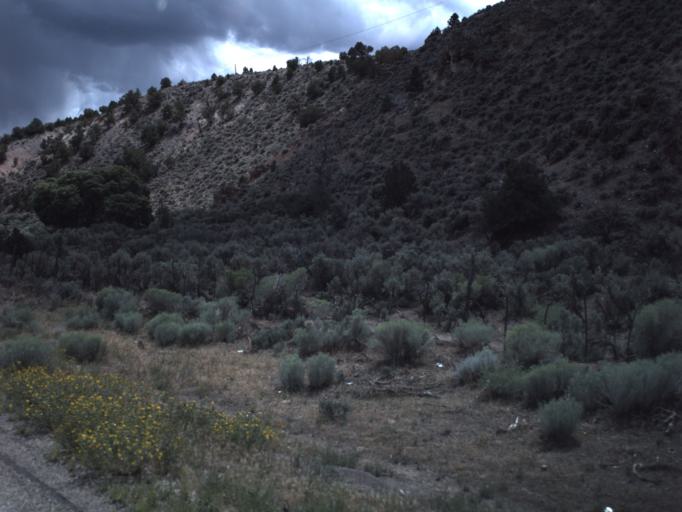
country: US
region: Utah
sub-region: Piute County
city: Junction
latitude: 38.2033
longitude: -112.1596
